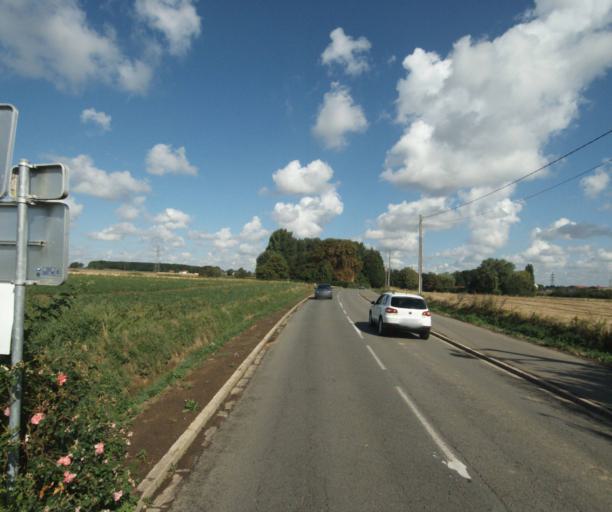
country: FR
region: Nord-Pas-de-Calais
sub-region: Departement du Nord
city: Sailly-lez-Lannoy
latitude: 50.6524
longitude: 3.2218
